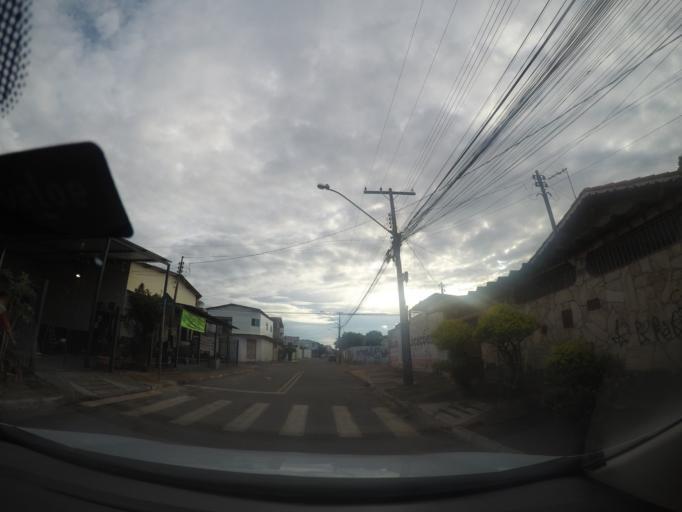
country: BR
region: Goias
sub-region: Goiania
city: Goiania
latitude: -16.6435
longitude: -49.3231
